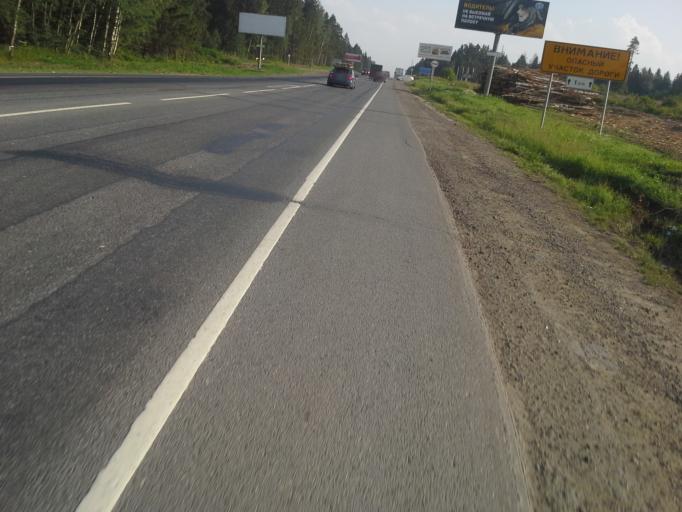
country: RU
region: Moskovskaya
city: Istra
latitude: 55.8431
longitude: 36.9238
